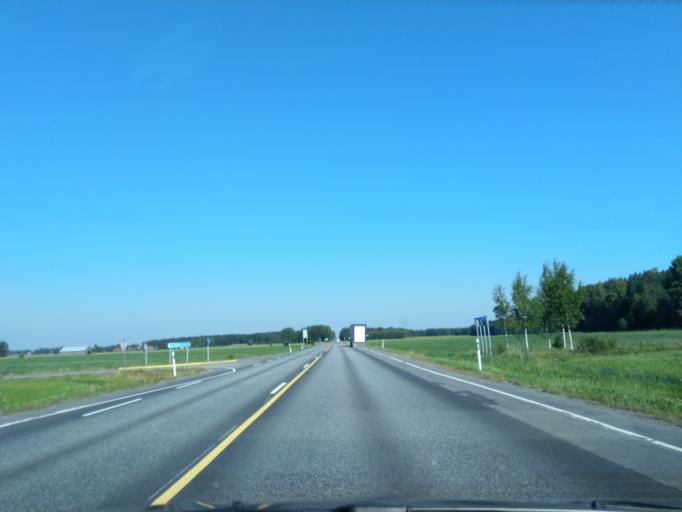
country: FI
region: Varsinais-Suomi
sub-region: Loimaa
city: Alastaro
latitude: 61.0618
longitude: 22.9379
